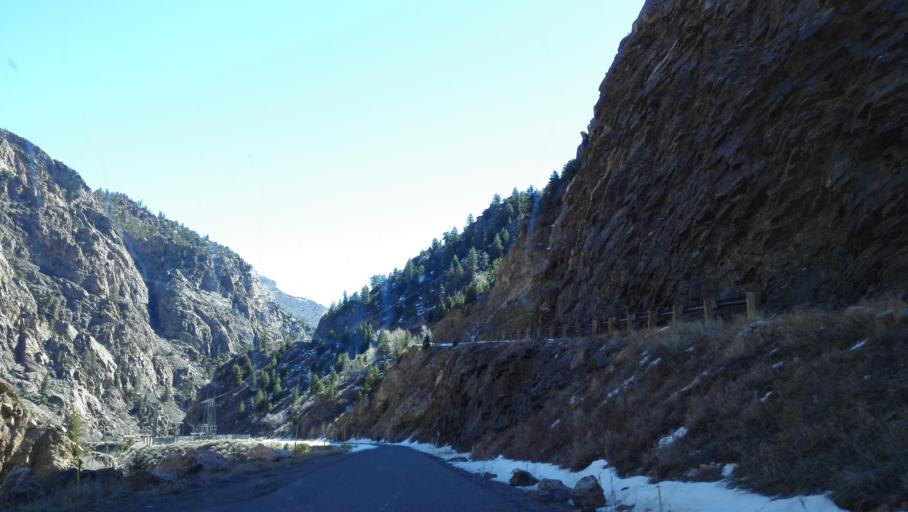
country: US
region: Colorado
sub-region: Montrose County
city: Montrose
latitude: 38.4517
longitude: -107.5487
